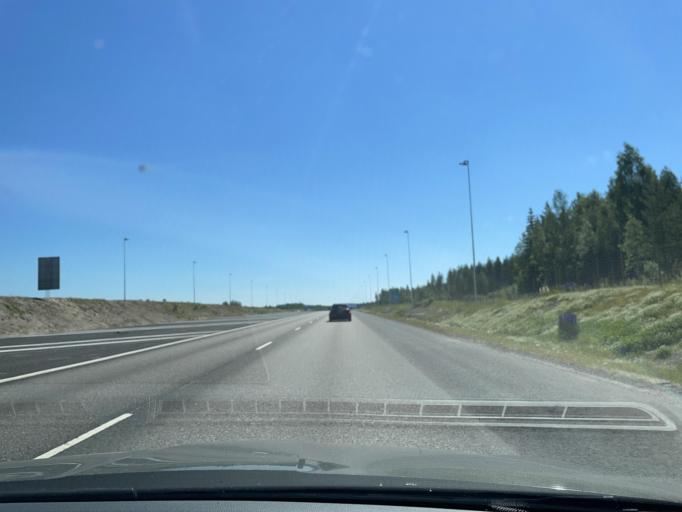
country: FI
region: Central Finland
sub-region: Jyvaeskylae
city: Jyvaeskylae
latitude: 62.4009
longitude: 25.7008
